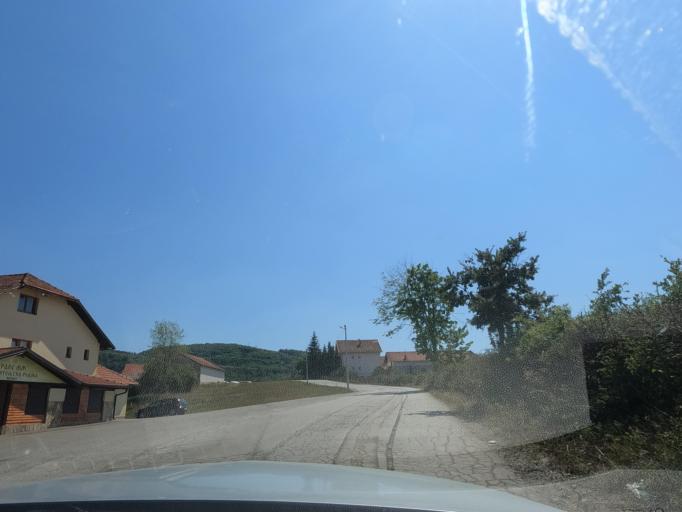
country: RS
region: Central Serbia
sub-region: Zlatiborski Okrug
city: Cajetina
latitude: 43.7901
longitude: 19.7658
